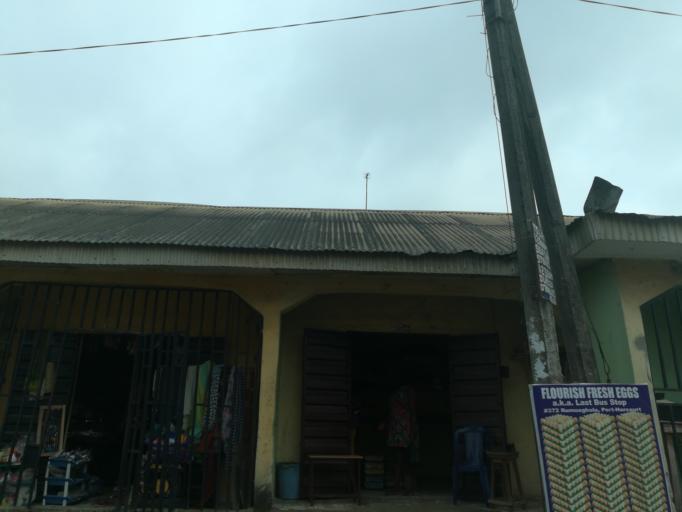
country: NG
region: Rivers
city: Port Harcourt
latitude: 4.8798
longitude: 6.9775
